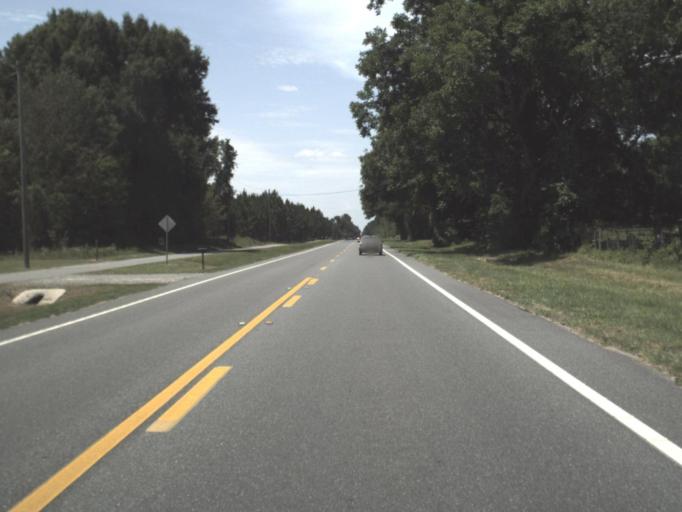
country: US
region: Florida
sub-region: Alachua County
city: High Springs
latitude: 29.9368
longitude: -82.8603
